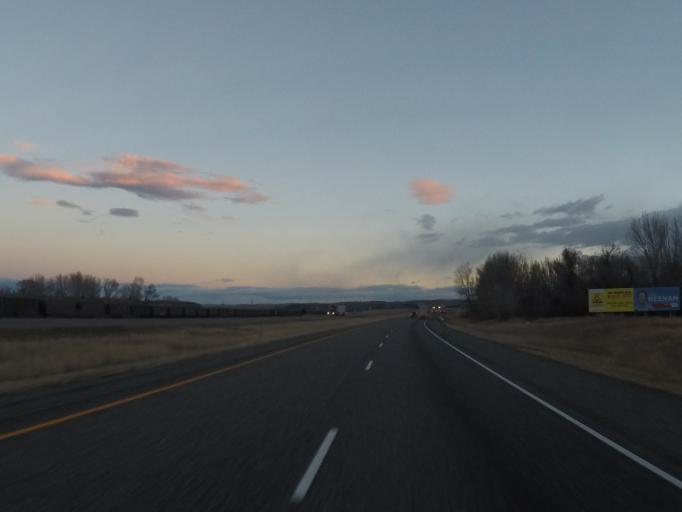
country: US
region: Montana
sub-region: Sweet Grass County
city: Big Timber
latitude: 45.7766
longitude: -109.8008
